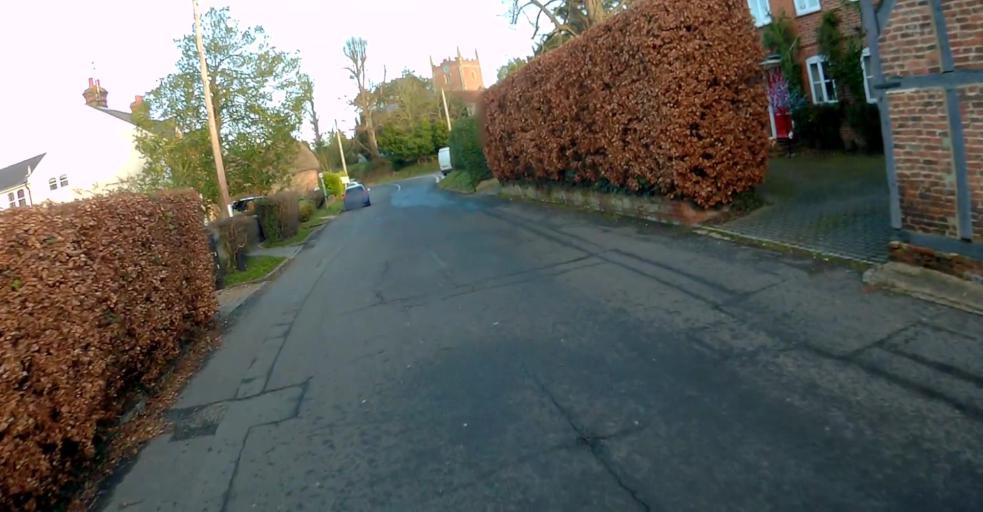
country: GB
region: England
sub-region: Hampshire
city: Old Basing
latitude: 51.2712
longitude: -1.0486
